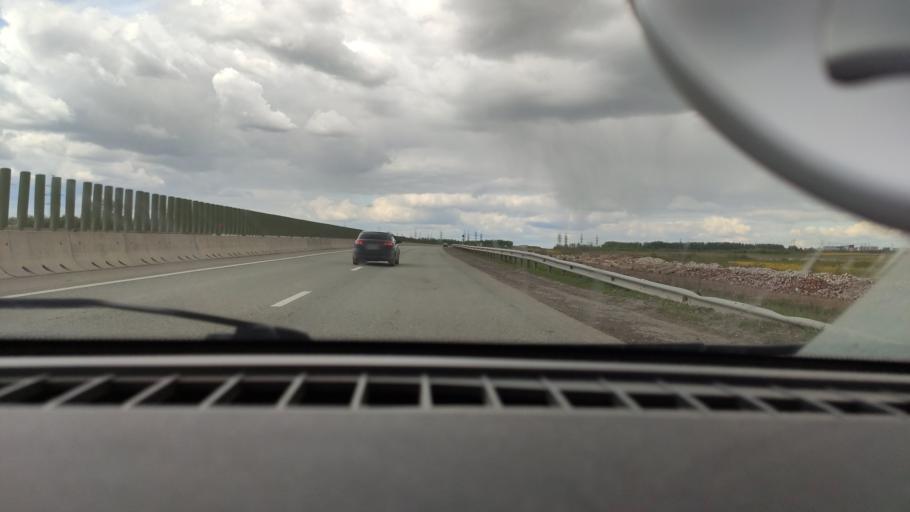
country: RU
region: Perm
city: Ferma
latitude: 57.9307
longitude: 56.3214
